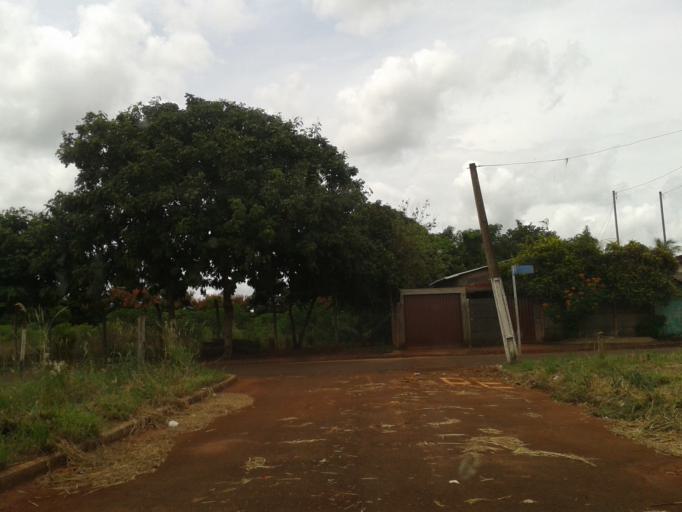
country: BR
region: Minas Gerais
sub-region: Centralina
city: Centralina
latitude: -18.5816
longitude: -49.2096
